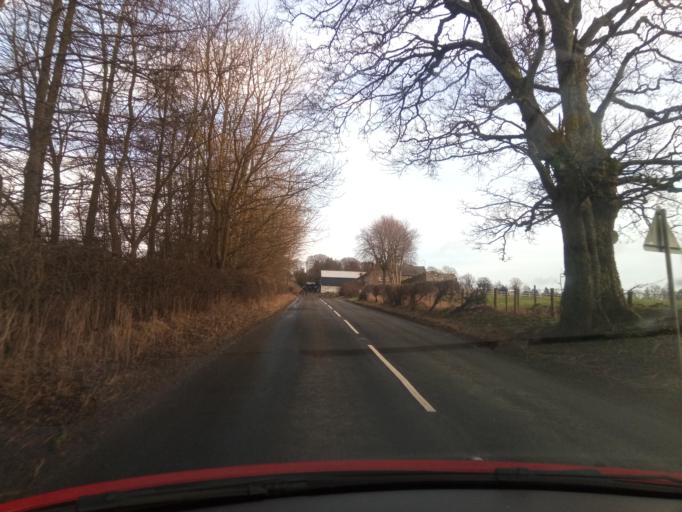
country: GB
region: England
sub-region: Northumberland
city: Corbridge
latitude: 55.1017
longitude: -2.0215
